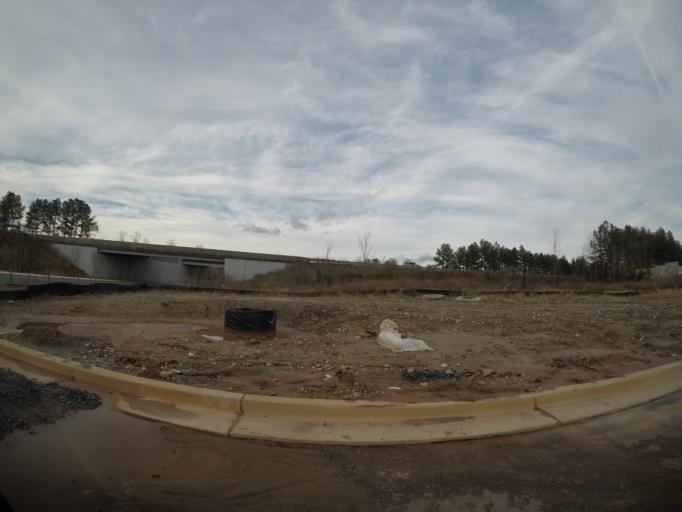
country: US
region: Maryland
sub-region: Anne Arundel County
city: Odenton
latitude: 39.0998
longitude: -76.7069
